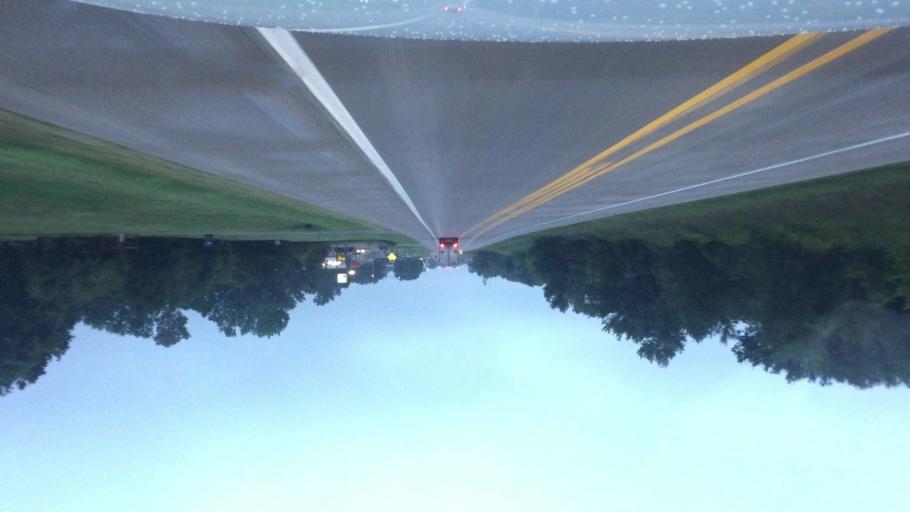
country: US
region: Kansas
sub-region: Neosho County
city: Chanute
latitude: 37.4961
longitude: -95.4705
